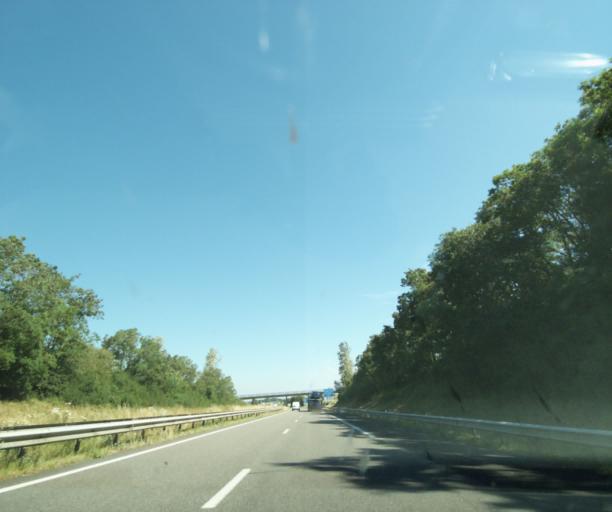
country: FR
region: Lorraine
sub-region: Departement des Vosges
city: Chatenois
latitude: 48.2569
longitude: 5.8653
